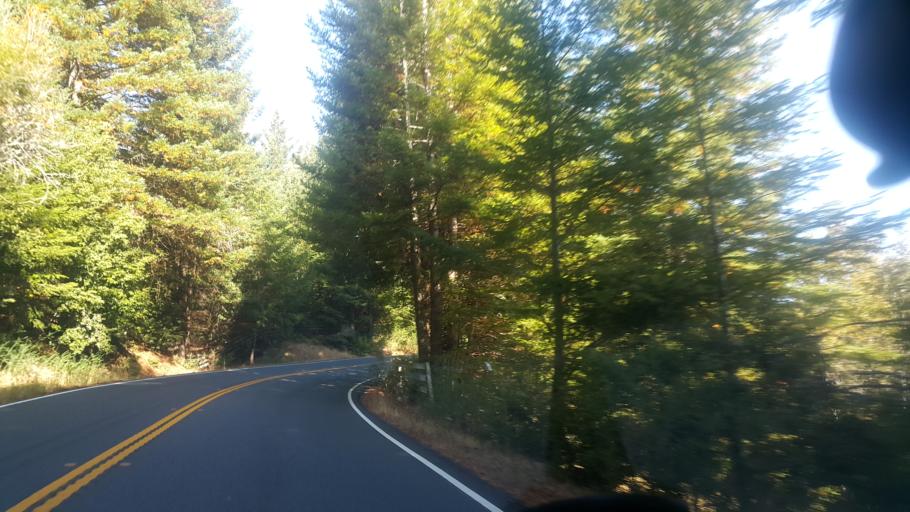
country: US
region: California
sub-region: Mendocino County
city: Fort Bragg
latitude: 39.3562
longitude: -123.6161
